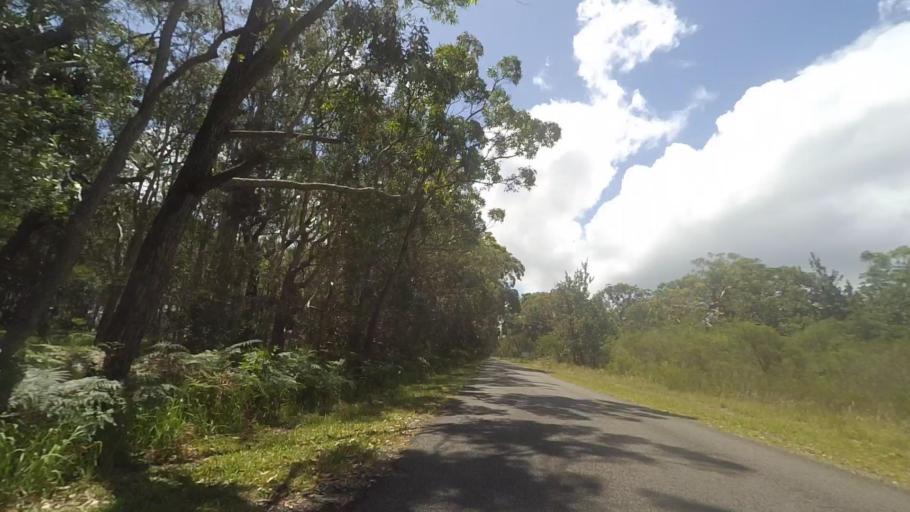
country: AU
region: New South Wales
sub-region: Great Lakes
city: Bulahdelah
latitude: -32.5149
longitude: 152.3223
